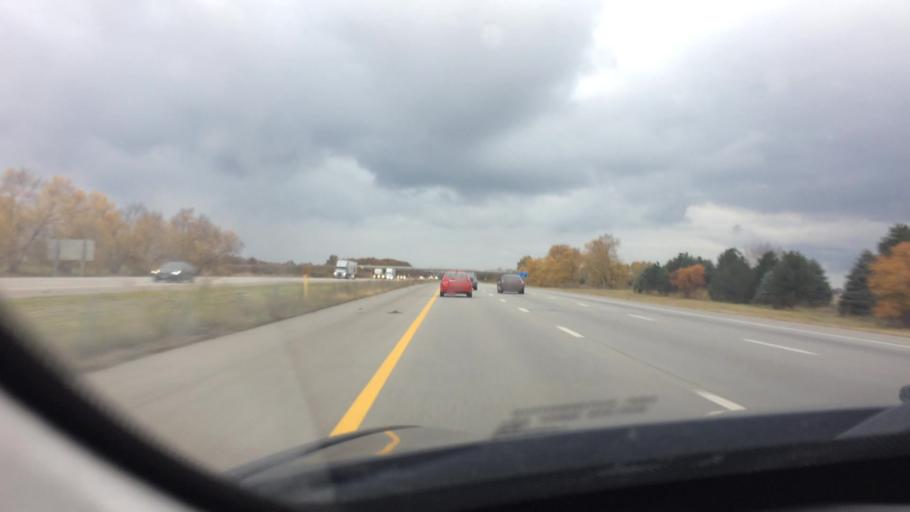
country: US
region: Ohio
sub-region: Wood County
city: Bowling Green
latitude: 41.3209
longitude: -83.6262
